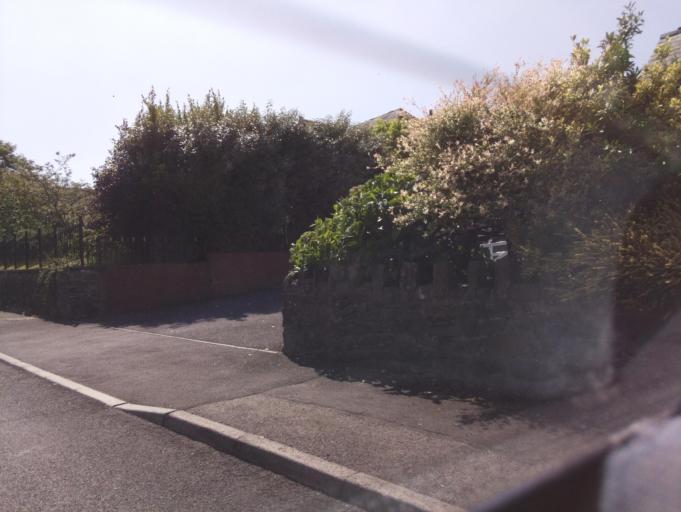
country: GB
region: Wales
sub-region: Caerphilly County Borough
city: Caerphilly
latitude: 51.5656
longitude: -3.2303
